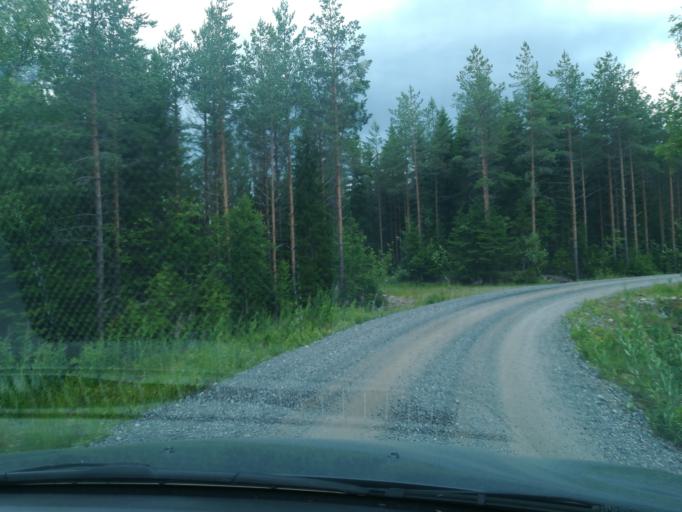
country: FI
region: Southern Savonia
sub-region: Mikkeli
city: Mikkeli
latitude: 61.6732
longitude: 27.1194
